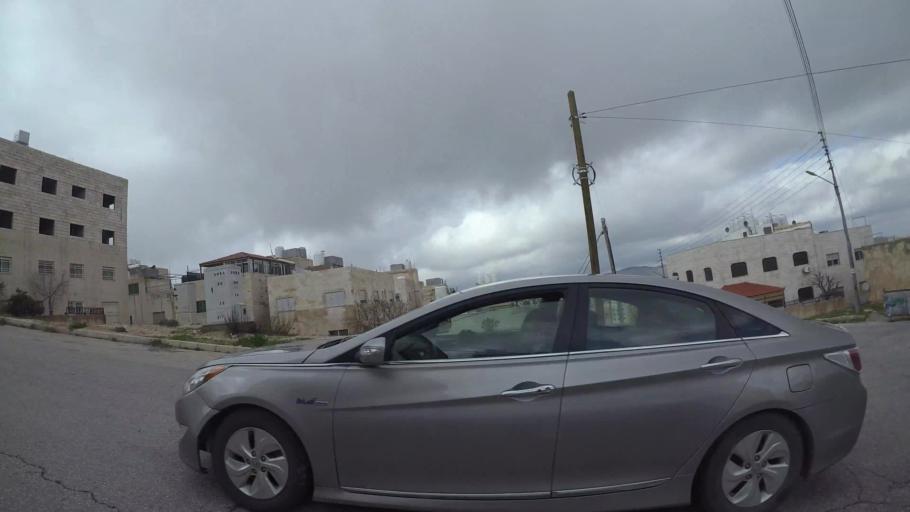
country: JO
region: Amman
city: Al Jubayhah
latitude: 32.0682
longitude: 35.8841
